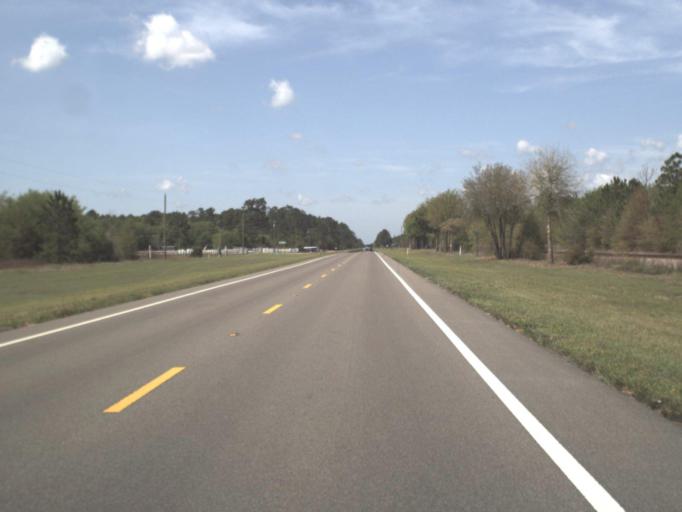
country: US
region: Florida
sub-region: Santa Rosa County
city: East Milton
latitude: 30.6945
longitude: -86.8042
